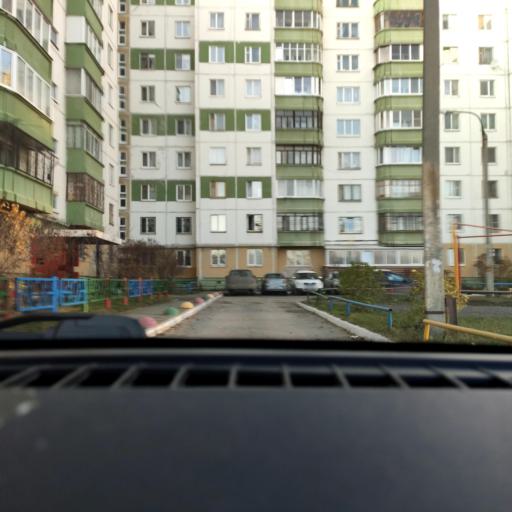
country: RU
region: Perm
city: Kondratovo
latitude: 58.0049
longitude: 56.1119
